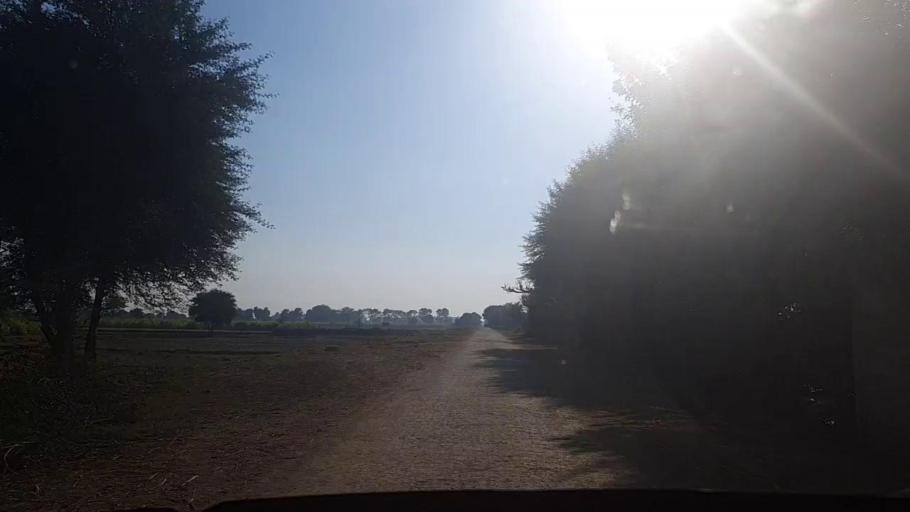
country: PK
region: Sindh
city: Gambat
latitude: 27.3655
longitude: 68.4604
